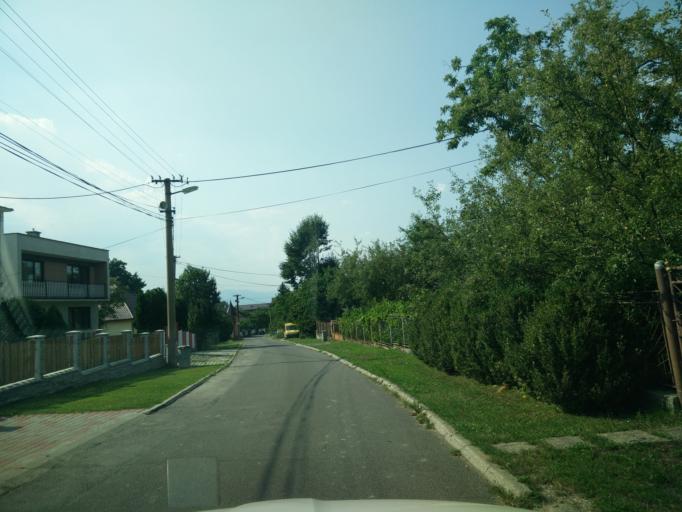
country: SK
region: Nitriansky
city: Prievidza
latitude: 48.7275
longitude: 18.6296
